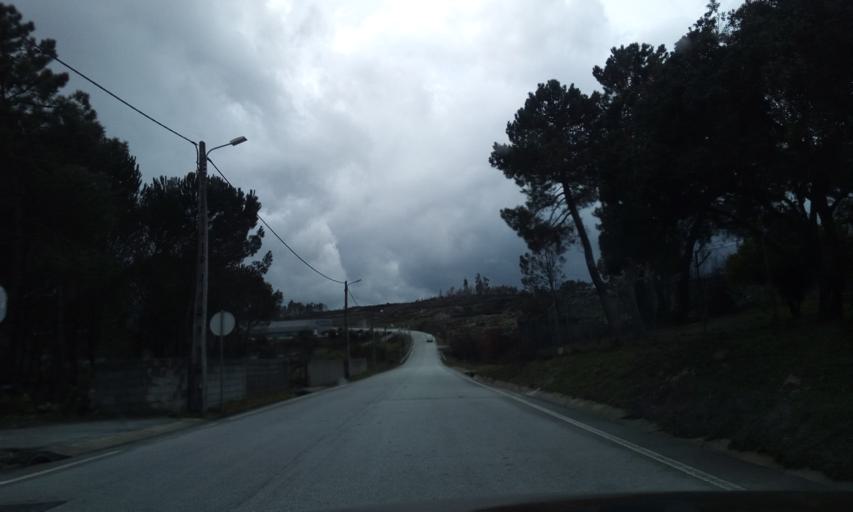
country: PT
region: Viseu
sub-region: Mangualde
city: Mangualde
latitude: 40.6015
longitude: -7.7962
